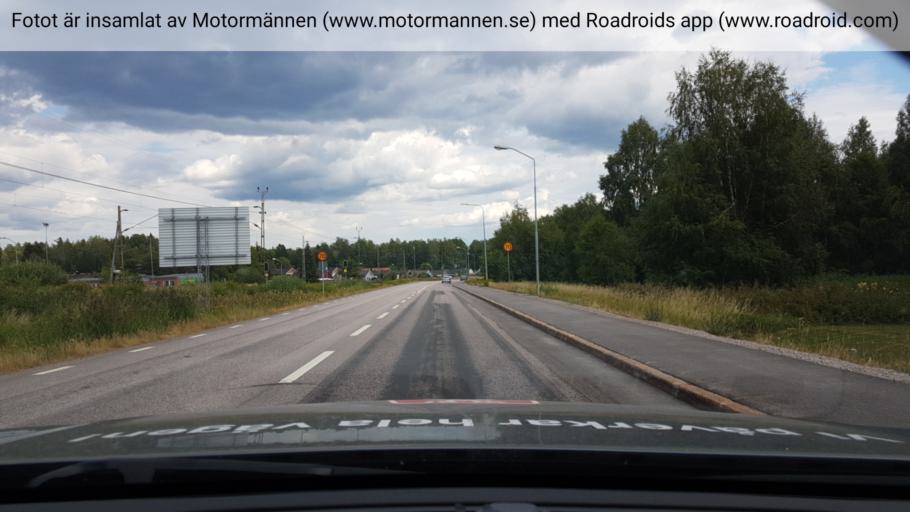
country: SE
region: Uppsala
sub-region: Heby Kommun
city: Morgongava
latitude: 59.9323
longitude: 16.9646
